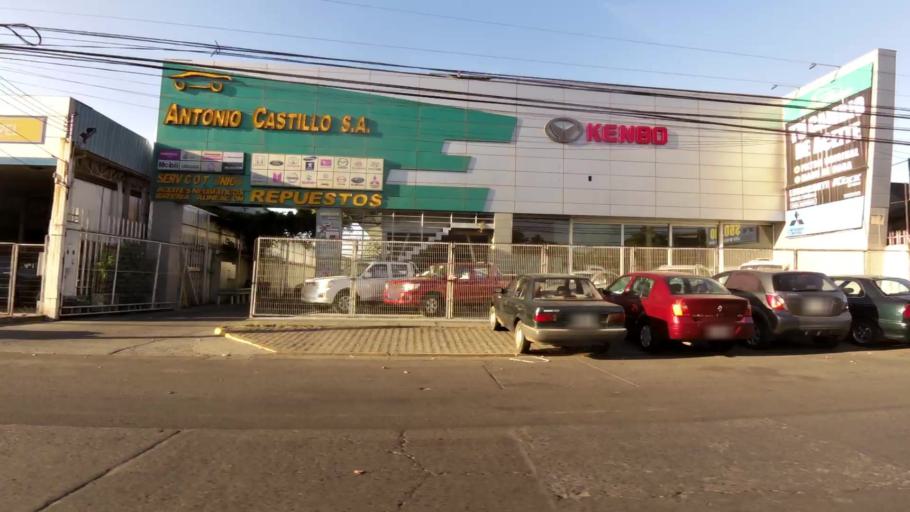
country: CL
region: Maule
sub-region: Provincia de Talca
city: Talca
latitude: -35.4278
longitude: -71.6434
